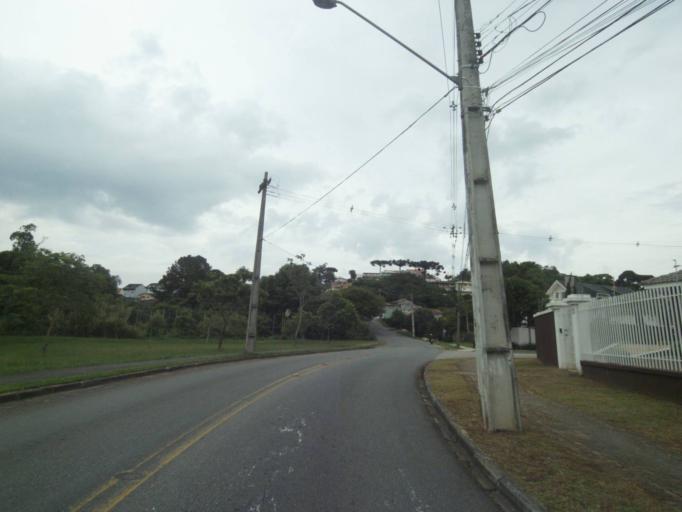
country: BR
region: Parana
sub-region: Curitiba
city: Curitiba
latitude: -25.4034
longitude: -49.3028
